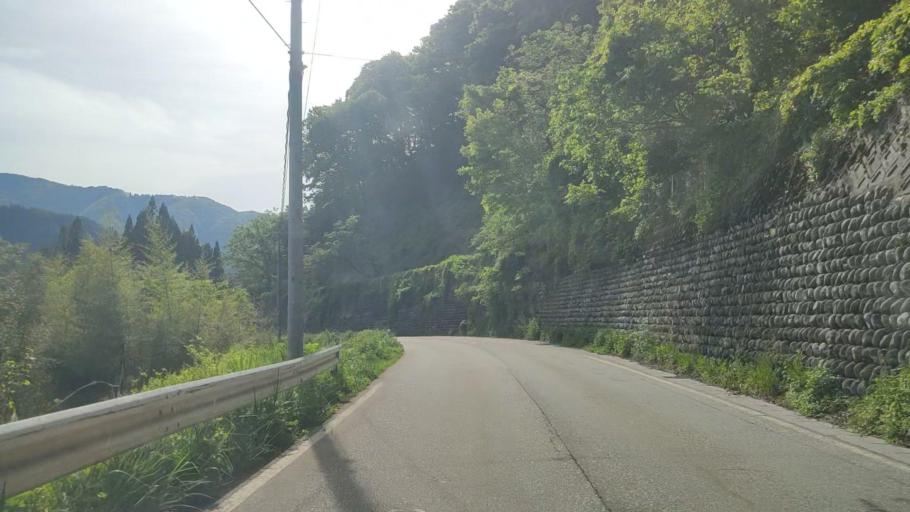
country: JP
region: Gifu
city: Takayama
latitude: 36.2973
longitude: 137.3637
